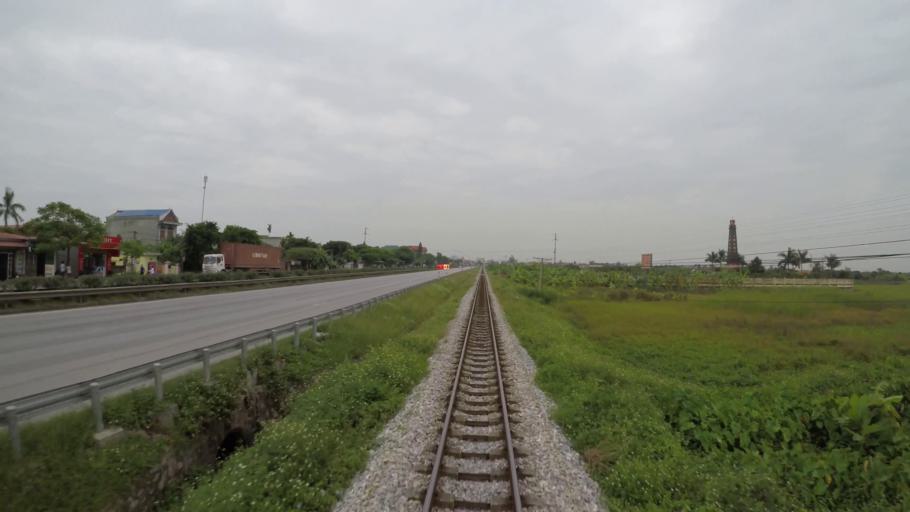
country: VN
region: Hai Duong
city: Phu Thai
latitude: 20.9687
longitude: 106.4525
